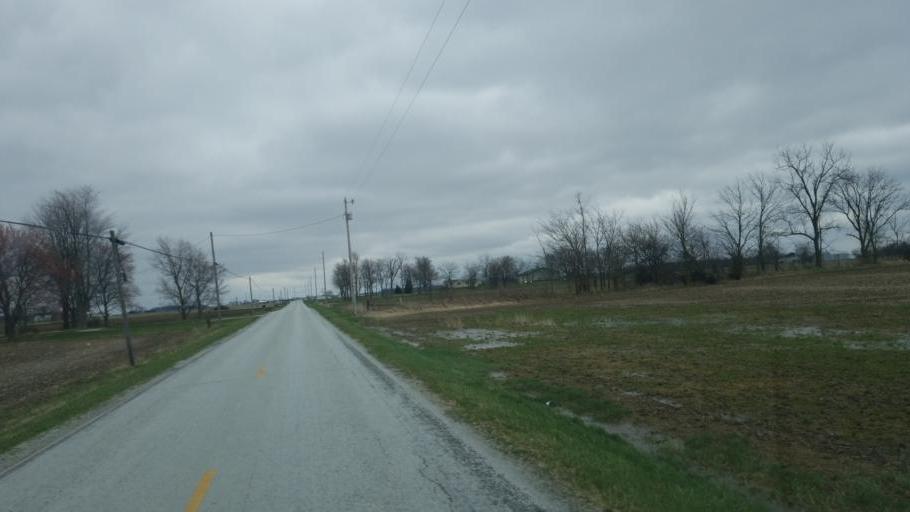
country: US
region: Ohio
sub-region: Hardin County
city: Kenton
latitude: 40.6582
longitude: -83.5437
